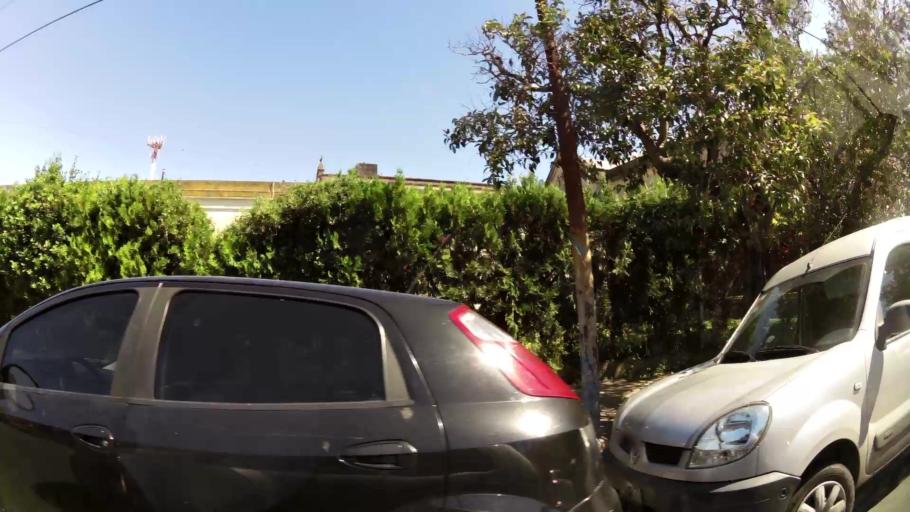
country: AR
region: Buenos Aires
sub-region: Partido de Quilmes
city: Quilmes
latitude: -34.7099
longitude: -58.2840
